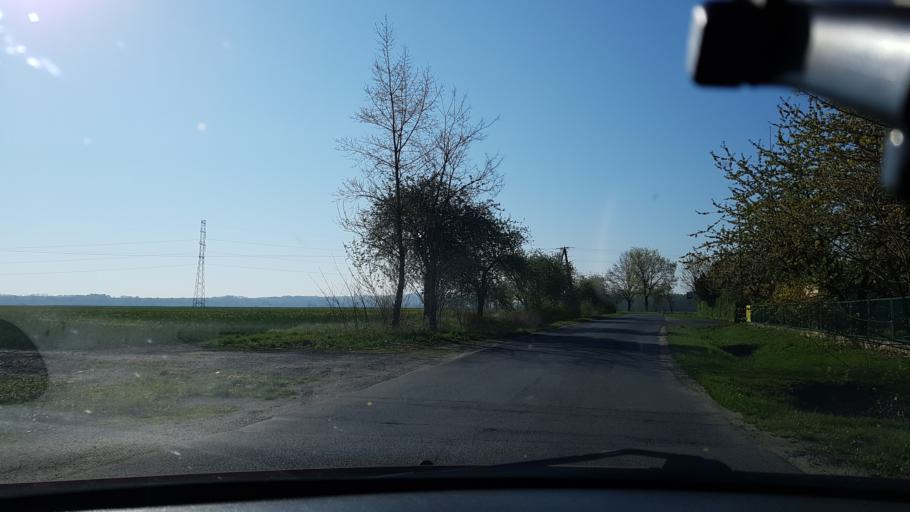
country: PL
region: Opole Voivodeship
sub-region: Powiat nyski
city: Nysa
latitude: 50.4292
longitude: 17.3065
